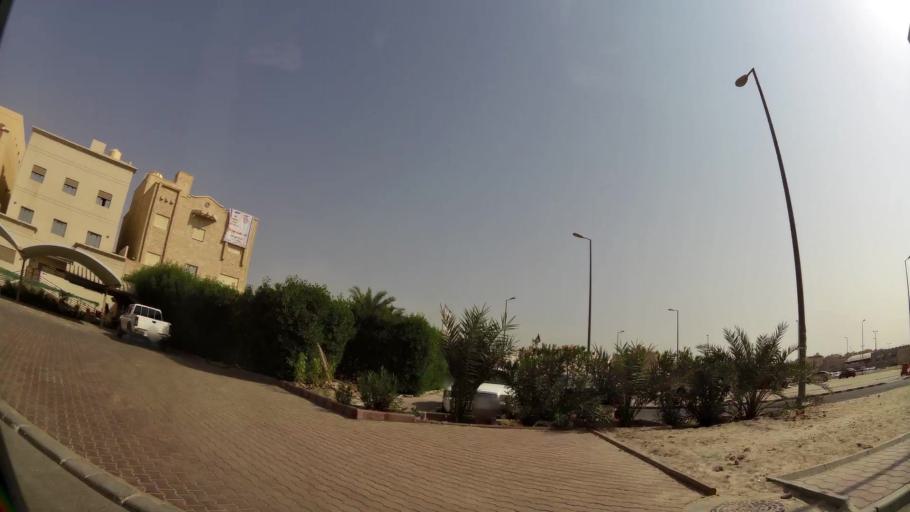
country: KW
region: Muhafazat al Jahra'
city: Al Jahra'
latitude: 29.3392
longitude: 47.7677
